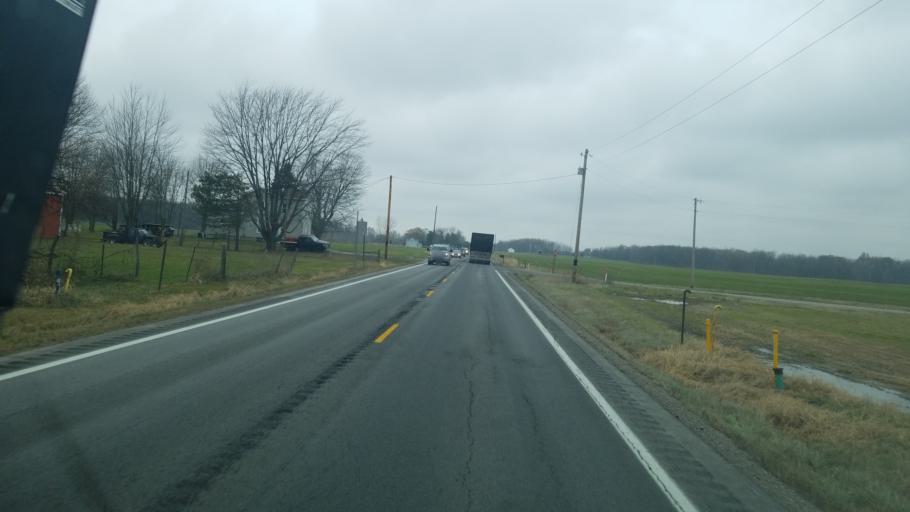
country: US
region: Ohio
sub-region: Huron County
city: Greenwich
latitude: 41.1064
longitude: -82.4986
